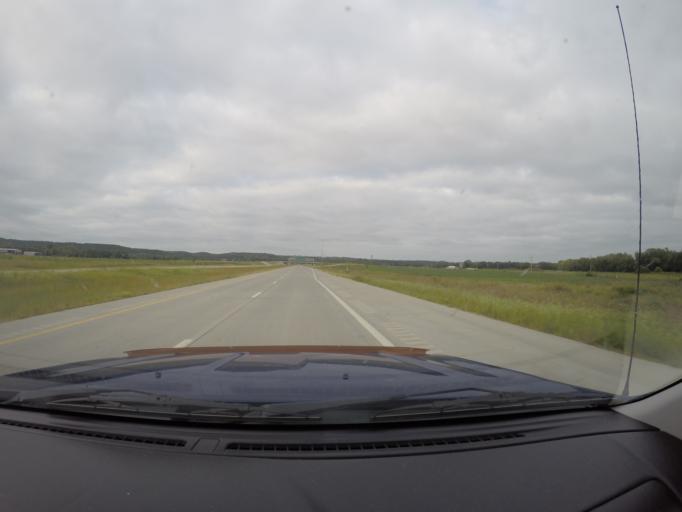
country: US
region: Kansas
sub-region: Riley County
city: Ogden
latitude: 39.1485
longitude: -96.6484
